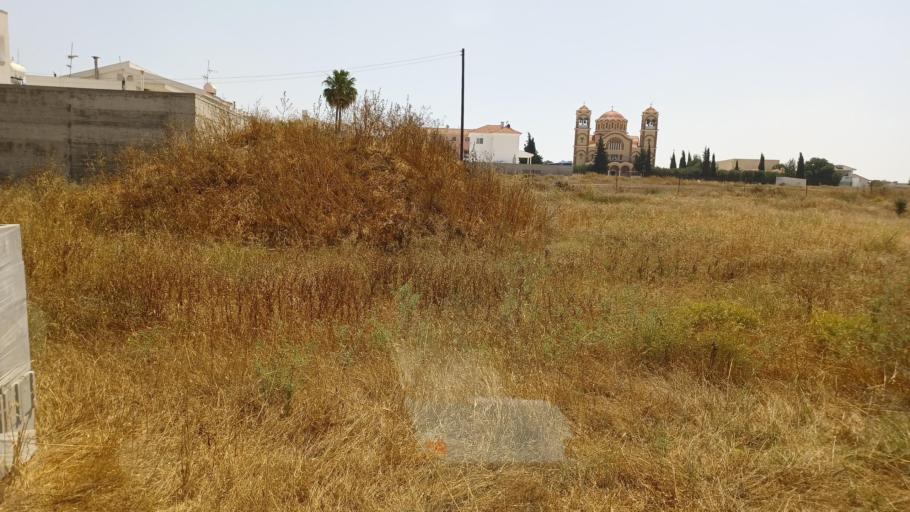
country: CY
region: Ammochostos
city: Paralimni
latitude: 35.0498
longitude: 33.9798
